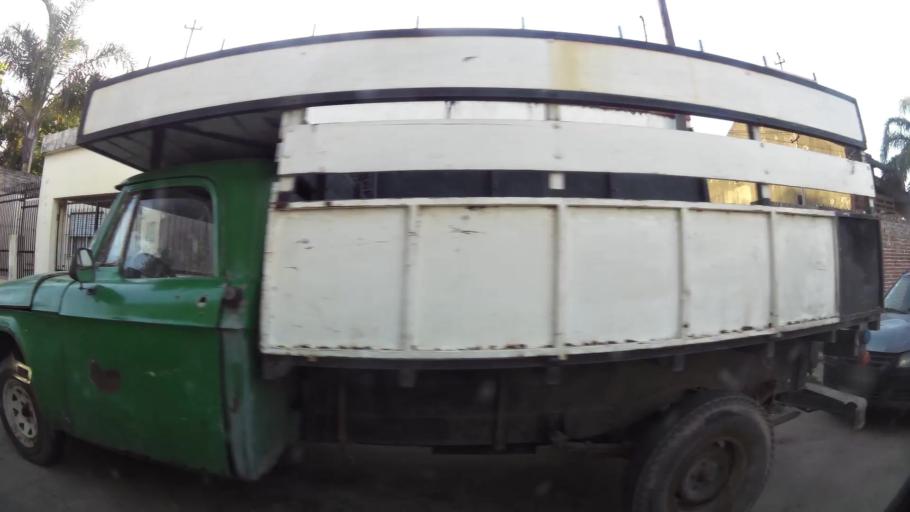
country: AR
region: Santa Fe
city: Santa Fe de la Vera Cruz
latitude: -31.5981
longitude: -60.6907
